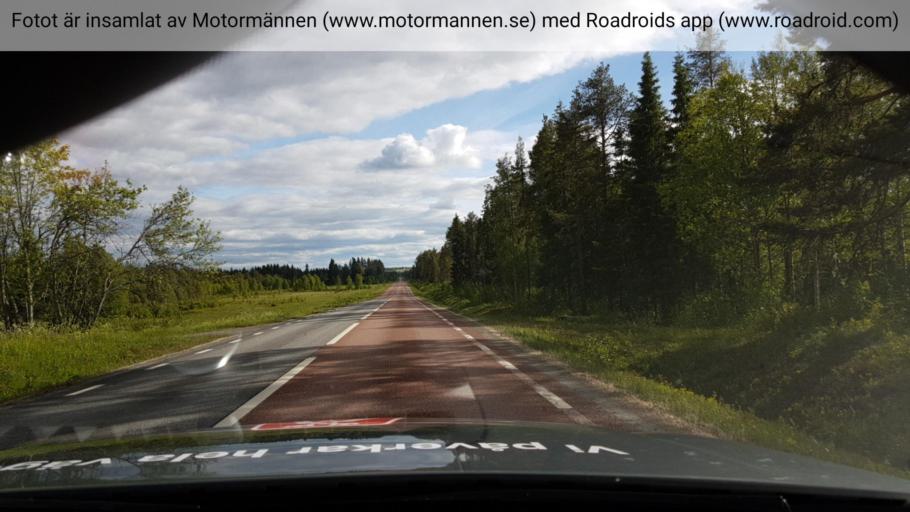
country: SE
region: Jaemtland
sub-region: Stroemsunds Kommun
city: Stroemsund
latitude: 63.7716
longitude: 15.5045
